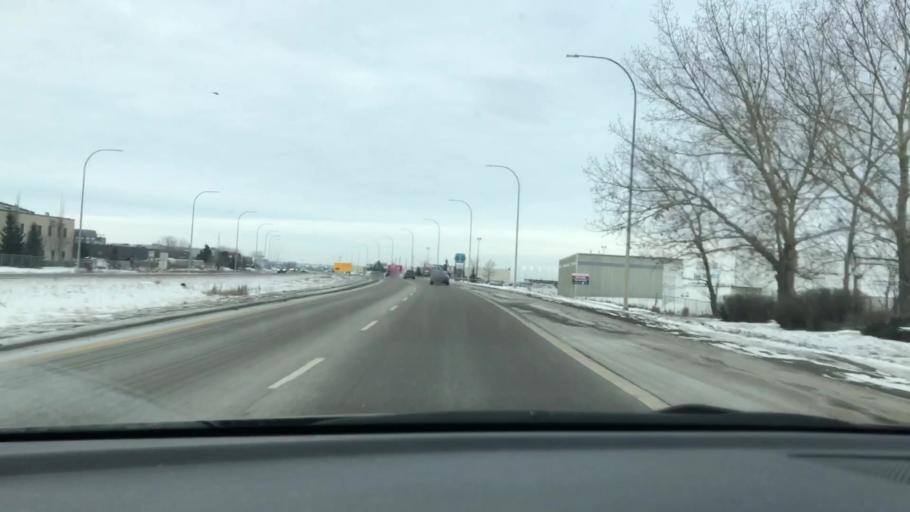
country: CA
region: Alberta
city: Edmonton
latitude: 53.5170
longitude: -113.4008
